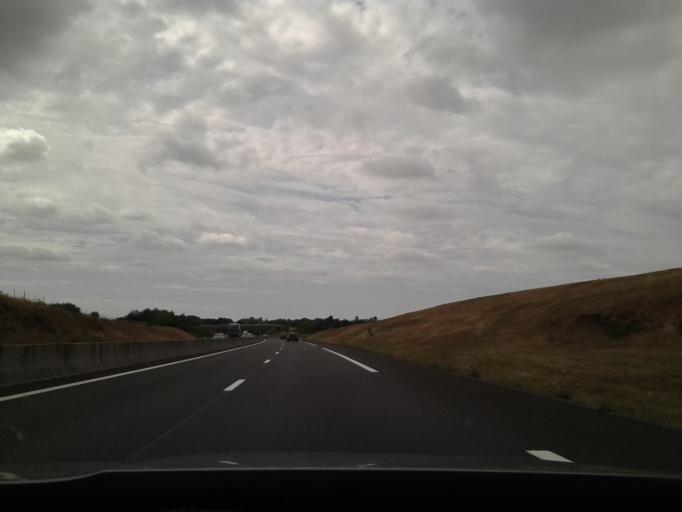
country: FR
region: Pays de la Loire
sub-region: Departement de la Sarthe
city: Arconnay
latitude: 48.3542
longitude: 0.0962
